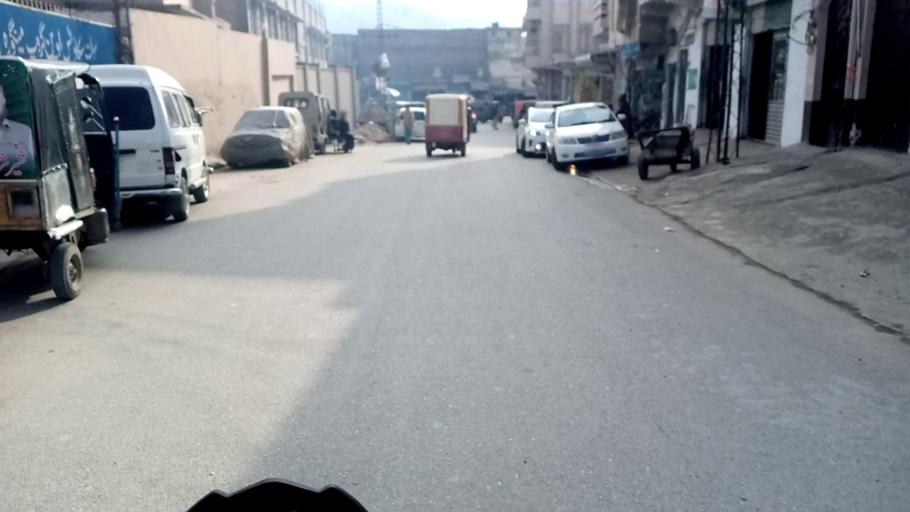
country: PK
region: Khyber Pakhtunkhwa
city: Mingora
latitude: 34.7717
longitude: 72.3658
